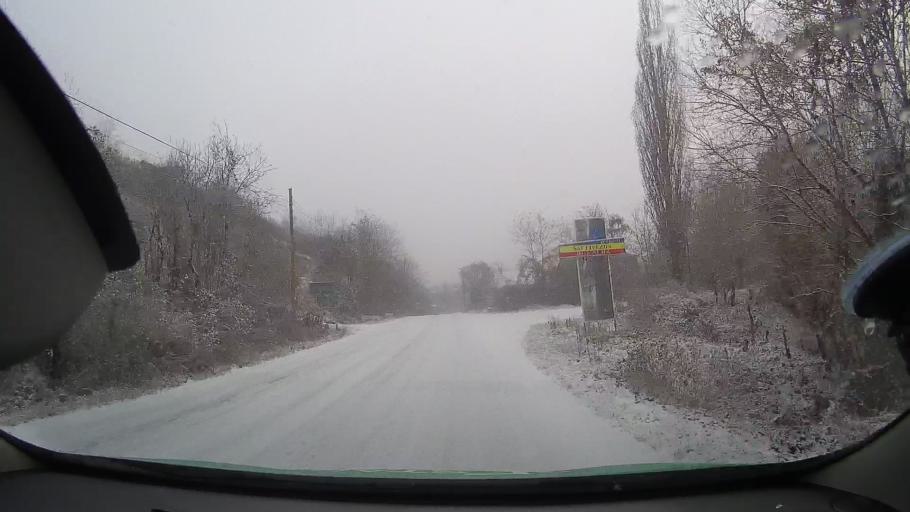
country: RO
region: Alba
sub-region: Comuna Livezile
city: Livezile
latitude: 46.3513
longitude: 23.6226
